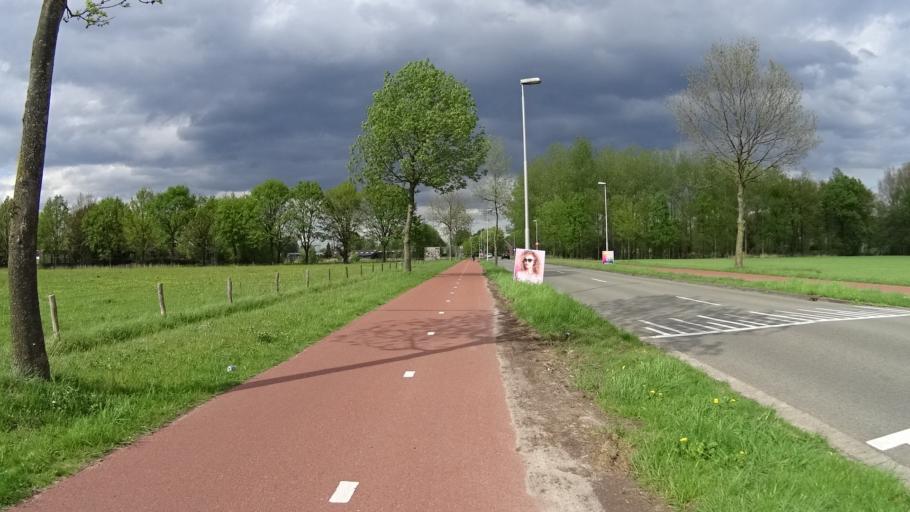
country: NL
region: North Brabant
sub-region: Gemeente Eindhoven
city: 't Hofke
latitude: 51.4572
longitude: 5.5272
